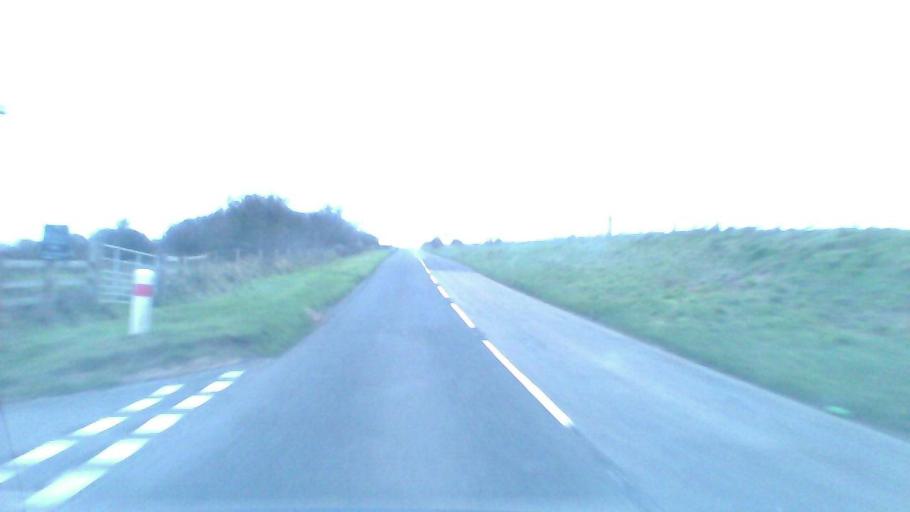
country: GB
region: England
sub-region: Isle of Wight
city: Newchurch
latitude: 50.6826
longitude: -1.2073
